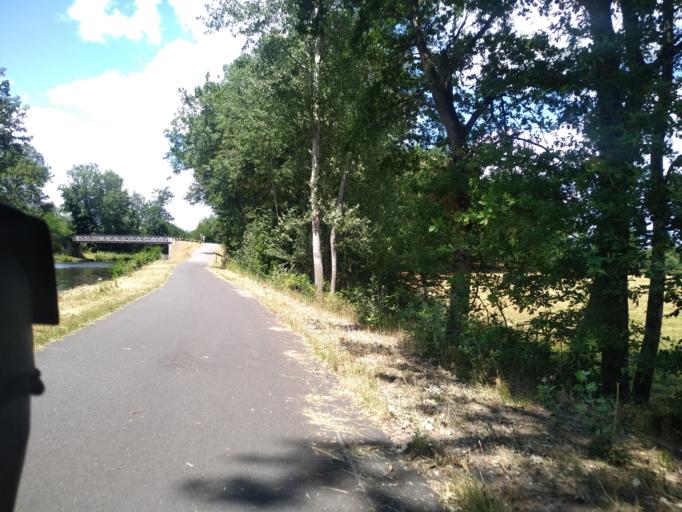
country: FR
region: Rhone-Alpes
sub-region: Departement de la Loire
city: Briennon
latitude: 46.1190
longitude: 4.0777
